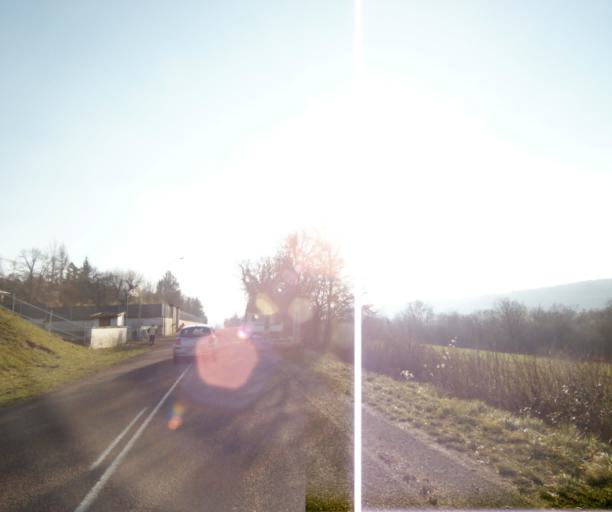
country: FR
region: Champagne-Ardenne
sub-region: Departement de la Haute-Marne
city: Chevillon
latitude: 48.5175
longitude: 5.1185
